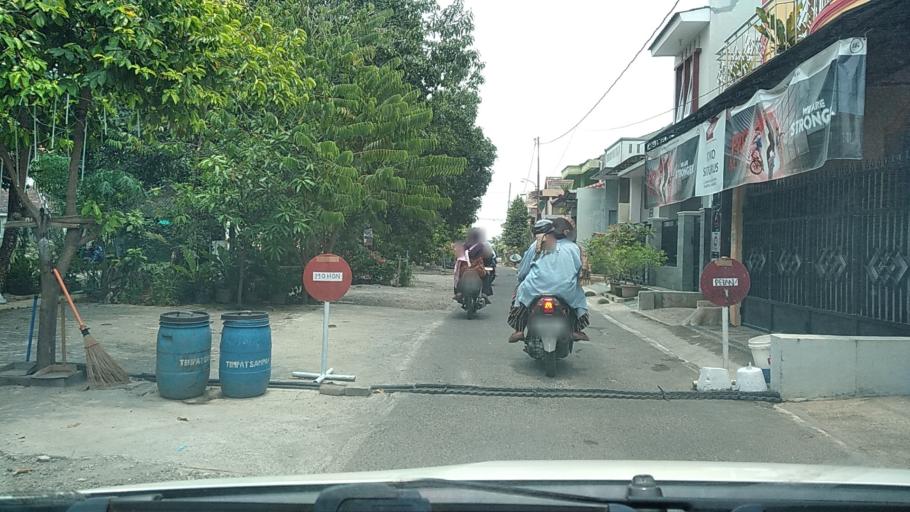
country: ID
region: Central Java
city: Semarang
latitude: -7.0091
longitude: 110.3706
